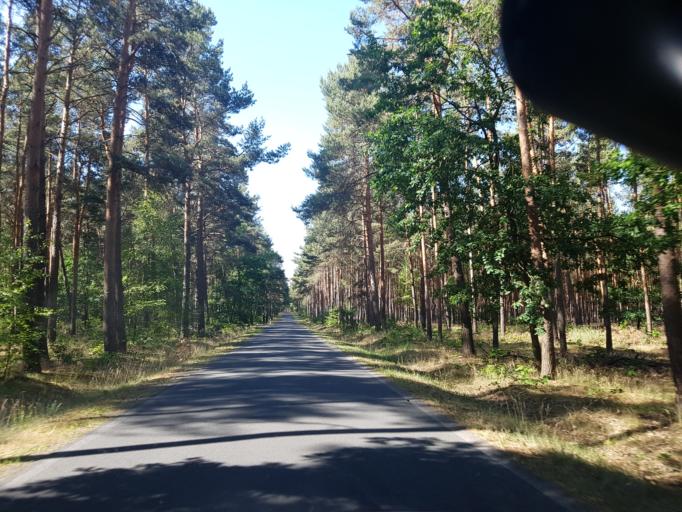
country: DE
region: Brandenburg
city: Treuenbrietzen
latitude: 52.0579
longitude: 12.8791
